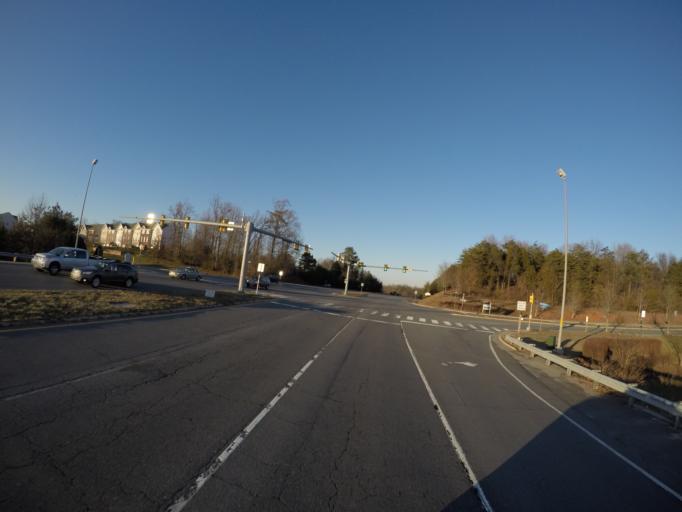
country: US
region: Virginia
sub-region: Loudoun County
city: Countryside
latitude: 39.0463
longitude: -77.4216
